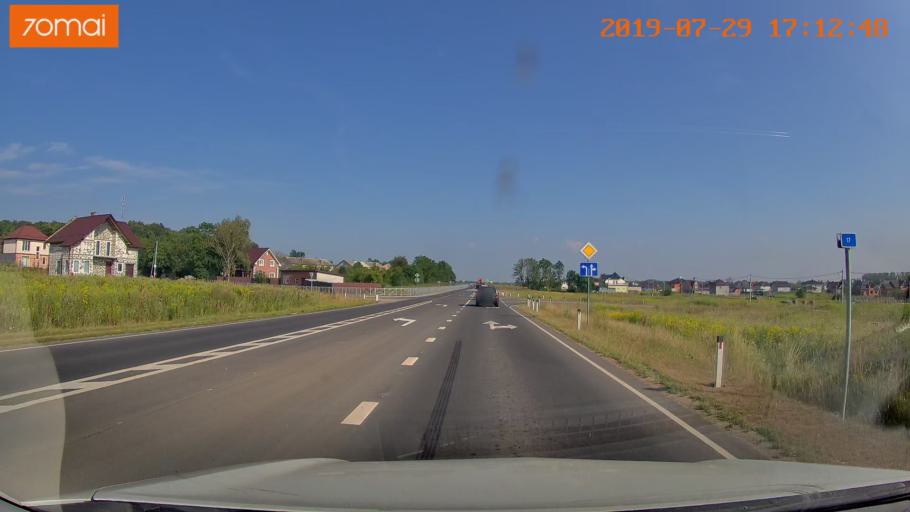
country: RU
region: Kaliningrad
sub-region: Gorod Kaliningrad
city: Kaliningrad
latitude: 54.7865
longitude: 20.4024
